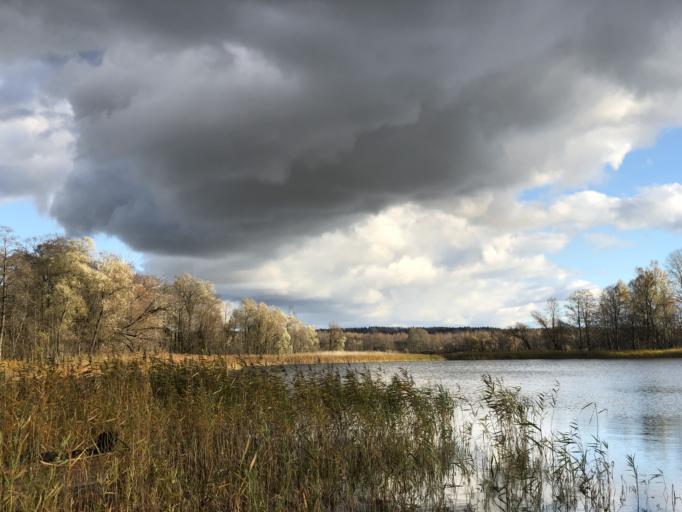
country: LT
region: Utenos apskritis
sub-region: Anyksciai
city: Anyksciai
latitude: 55.5278
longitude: 25.2832
